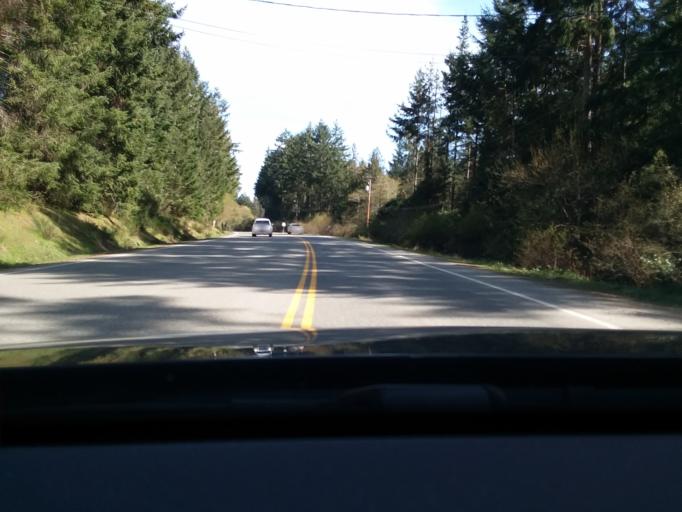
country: CA
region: British Columbia
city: North Saanich
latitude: 48.8520
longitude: -123.4598
